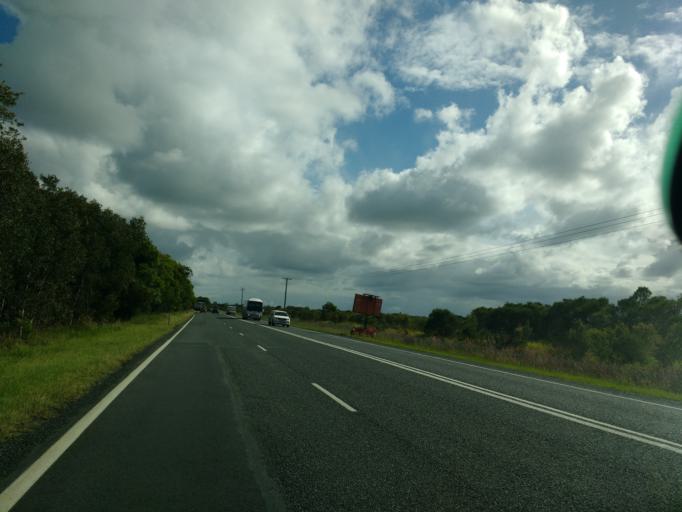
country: AU
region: New South Wales
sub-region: Richmond Valley
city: Evans Head
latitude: -29.0301
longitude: 153.4100
